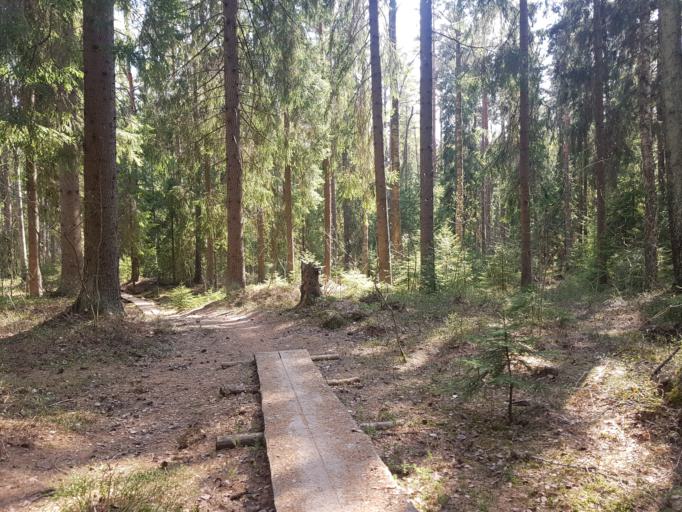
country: FI
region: Uusimaa
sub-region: Helsinki
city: Helsinki
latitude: 60.2675
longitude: 24.9174
